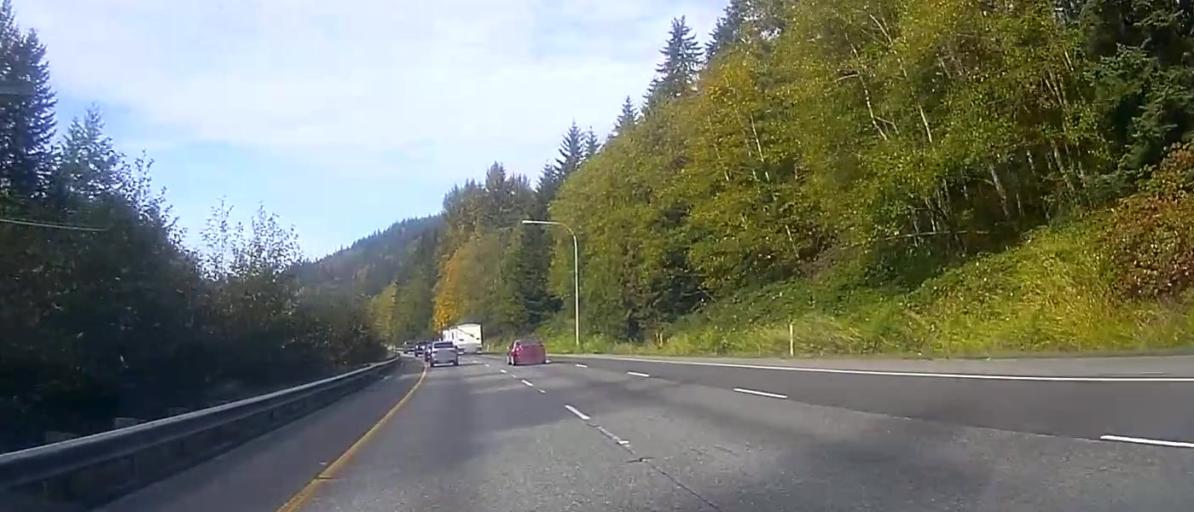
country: US
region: Washington
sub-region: Whatcom County
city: Geneva
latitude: 48.6901
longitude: -122.4059
